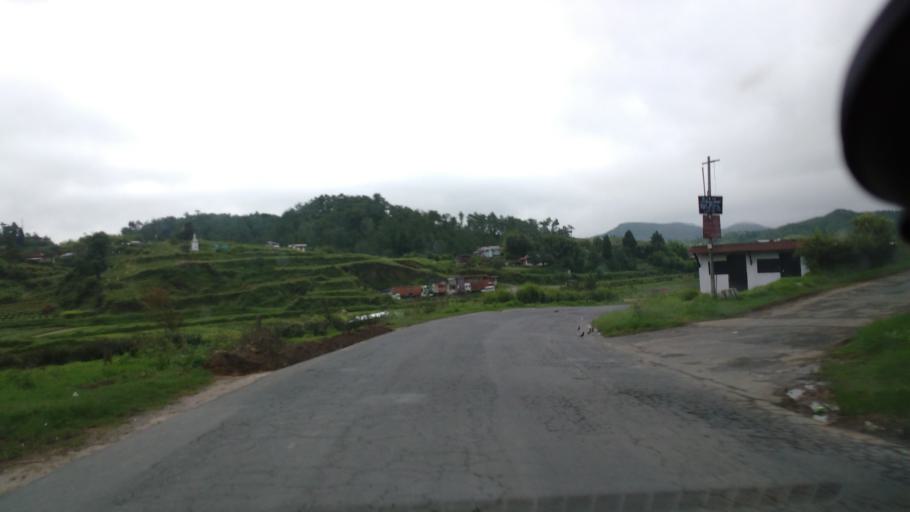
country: IN
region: Meghalaya
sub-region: East Khasi Hills
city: Shillong
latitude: 25.5141
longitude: 91.8114
